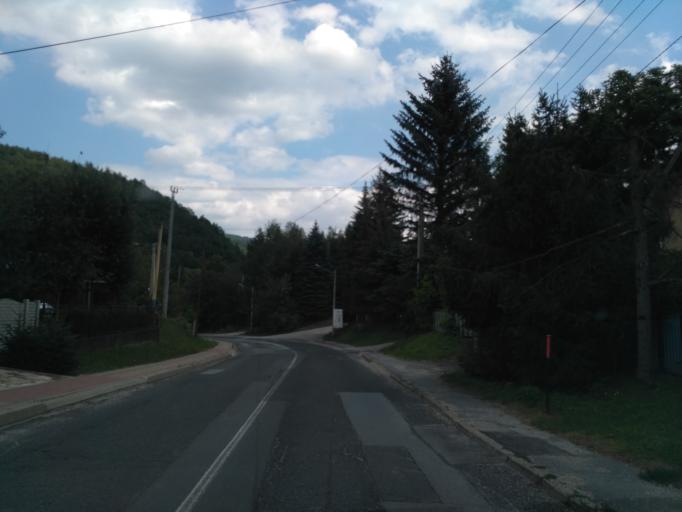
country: SK
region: Kosicky
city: Gelnica
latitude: 48.8928
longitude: 21.0156
